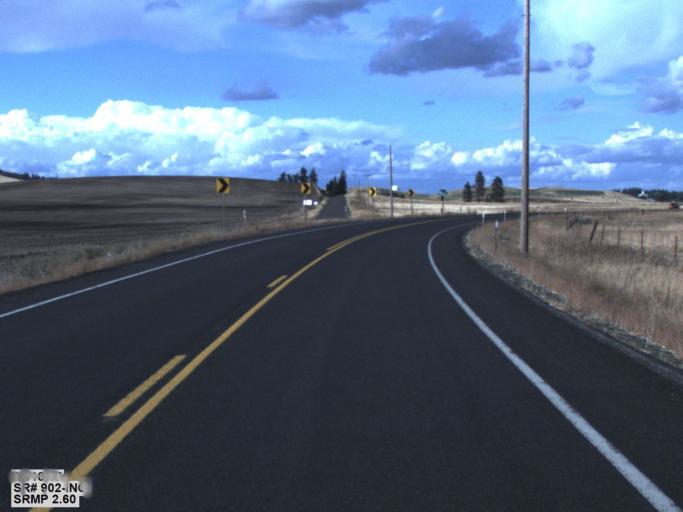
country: US
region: Washington
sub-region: Spokane County
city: Medical Lake
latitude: 47.5309
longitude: -117.7149
